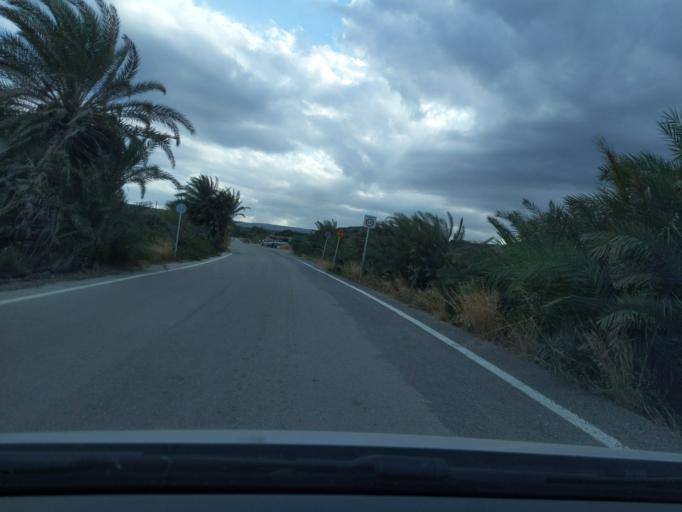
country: GR
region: Crete
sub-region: Nomos Lasithiou
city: Palekastro
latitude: 35.2553
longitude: 26.2536
